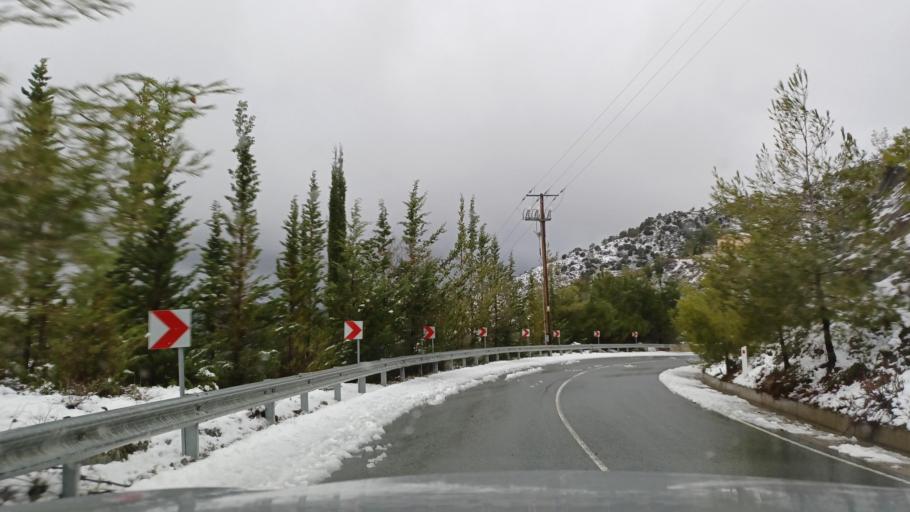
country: CY
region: Limassol
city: Pelendri
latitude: 34.8991
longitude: 32.9627
